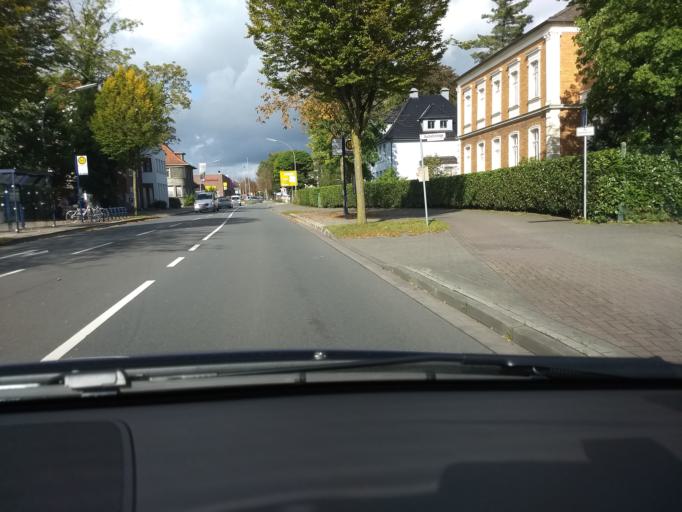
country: DE
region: North Rhine-Westphalia
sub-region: Regierungsbezirk Munster
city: Borken
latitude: 51.8448
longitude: 6.8637
